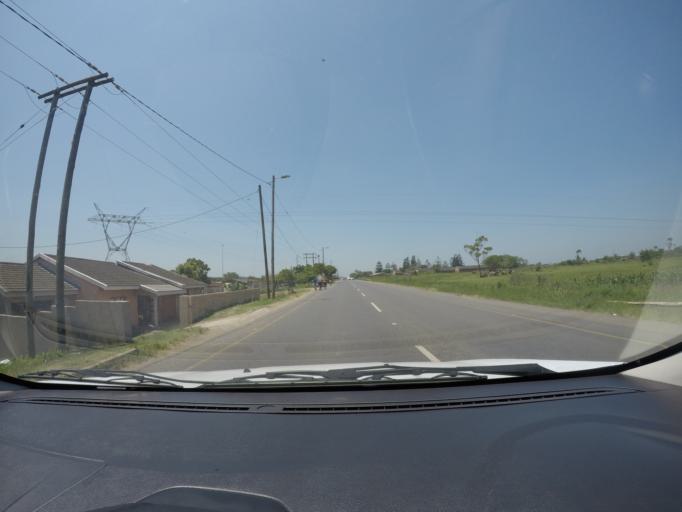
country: ZA
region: KwaZulu-Natal
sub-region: uThungulu District Municipality
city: eSikhawini
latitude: -28.8779
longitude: 31.8931
